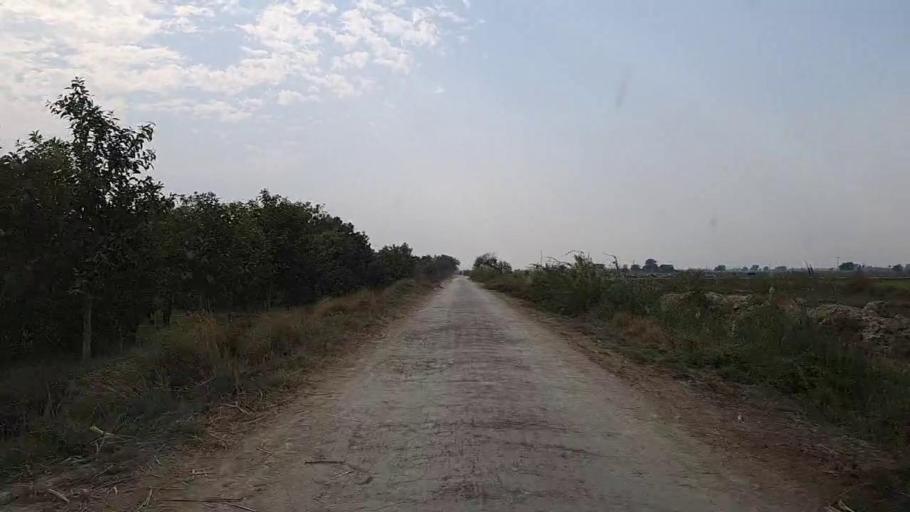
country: PK
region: Sindh
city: Mirwah Gorchani
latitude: 25.3718
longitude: 69.0755
